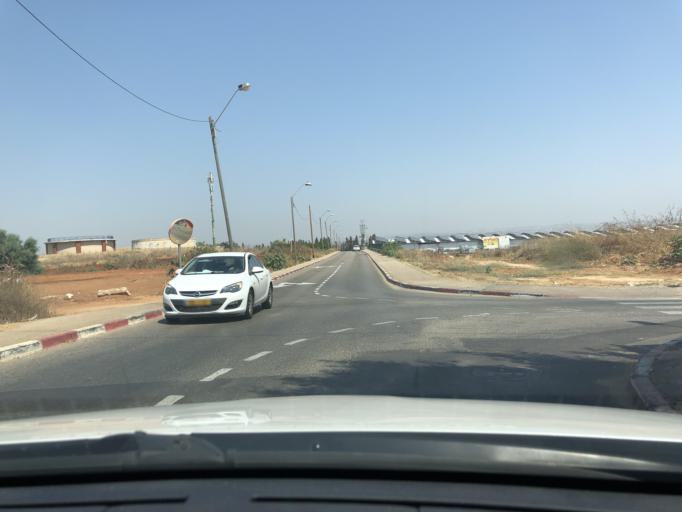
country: IL
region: Central District
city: Kfar Saba
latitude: 32.1648
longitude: 34.9126
